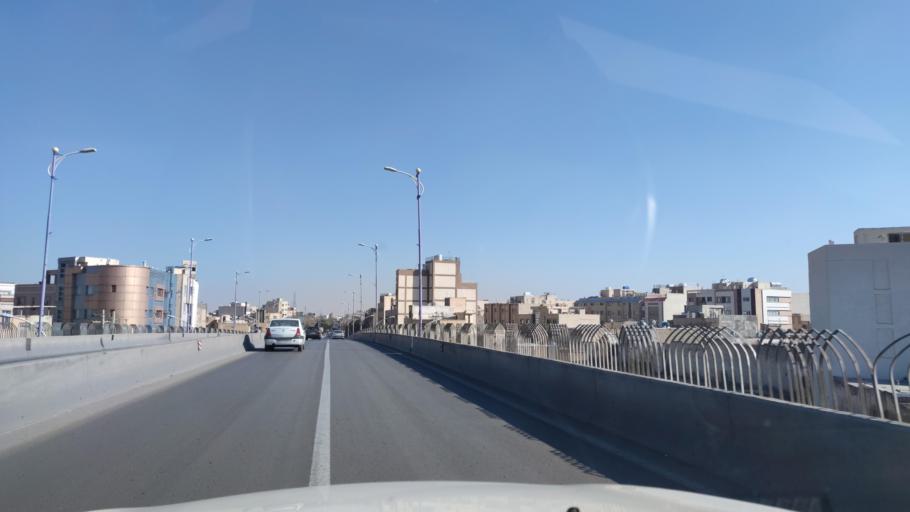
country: IR
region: Isfahan
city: Isfahan
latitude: 32.6791
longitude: 51.6724
